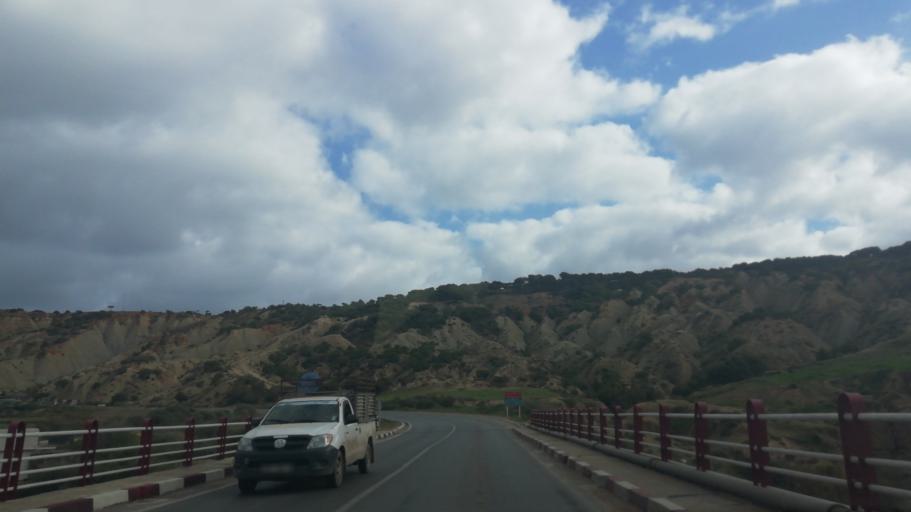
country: DZ
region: Relizane
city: Mazouna
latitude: 36.3038
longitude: 0.6703
